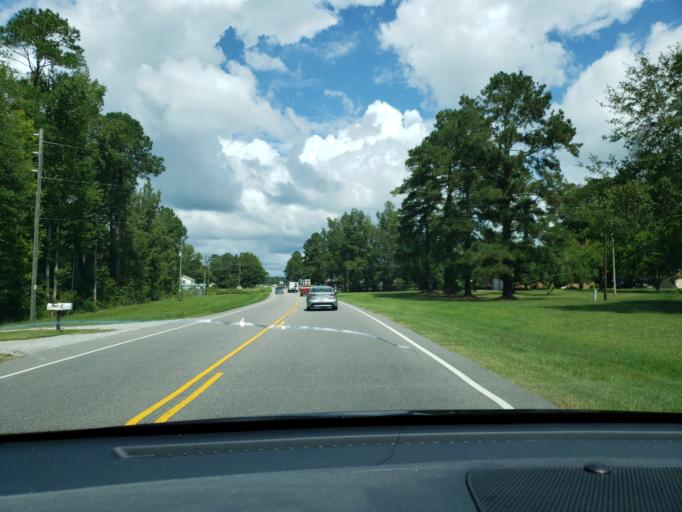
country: US
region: North Carolina
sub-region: Columbus County
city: Brunswick
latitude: 34.2675
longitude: -78.7420
